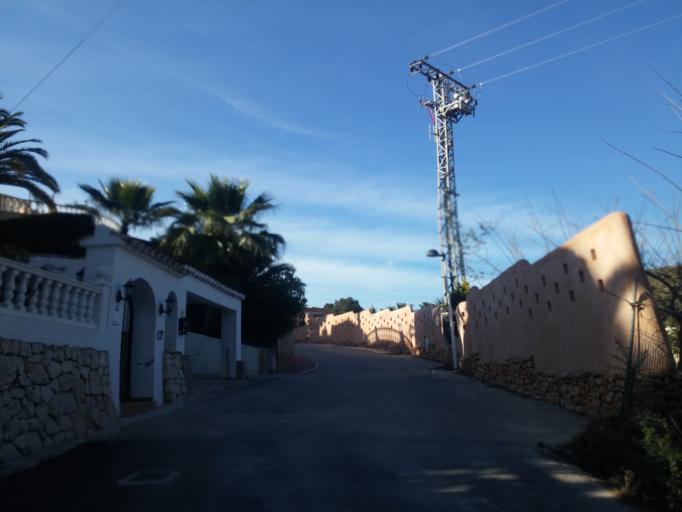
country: ES
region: Valencia
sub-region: Provincia de Alicante
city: Moraira
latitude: 38.6979
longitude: 0.1440
